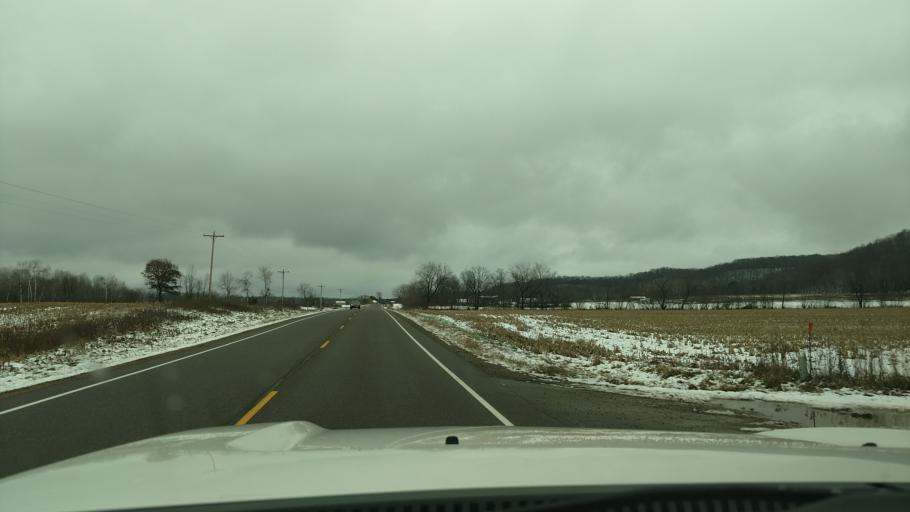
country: US
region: Wisconsin
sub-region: Dunn County
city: Colfax
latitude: 45.1385
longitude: -91.7763
